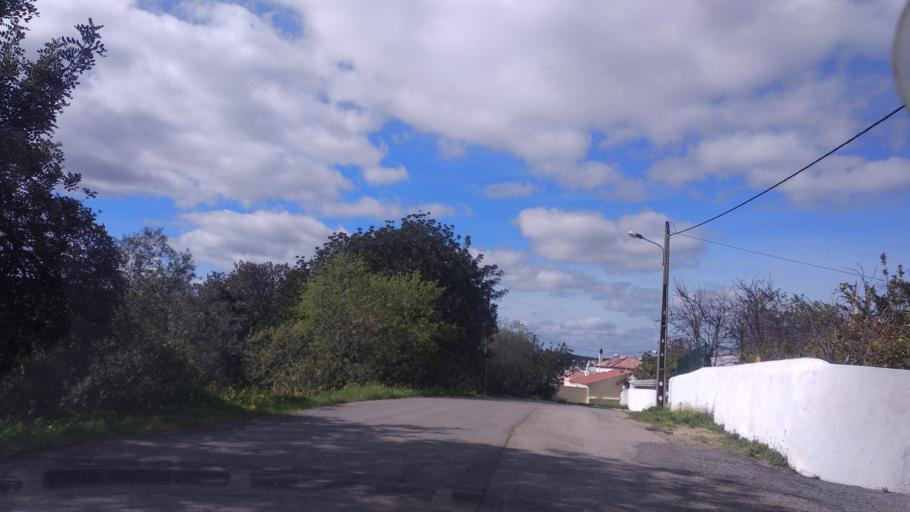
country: PT
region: Faro
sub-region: Sao Bras de Alportel
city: Sao Bras de Alportel
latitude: 37.1500
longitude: -7.9161
